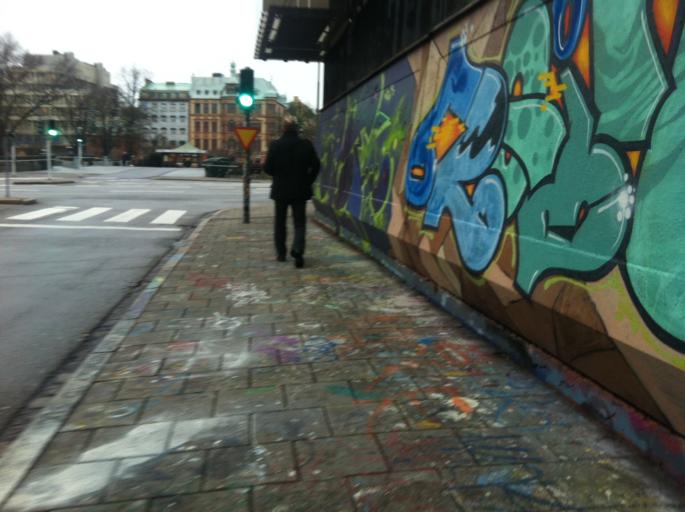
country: SE
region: Skane
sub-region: Malmo
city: Malmoe
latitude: 55.6001
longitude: 13.0050
